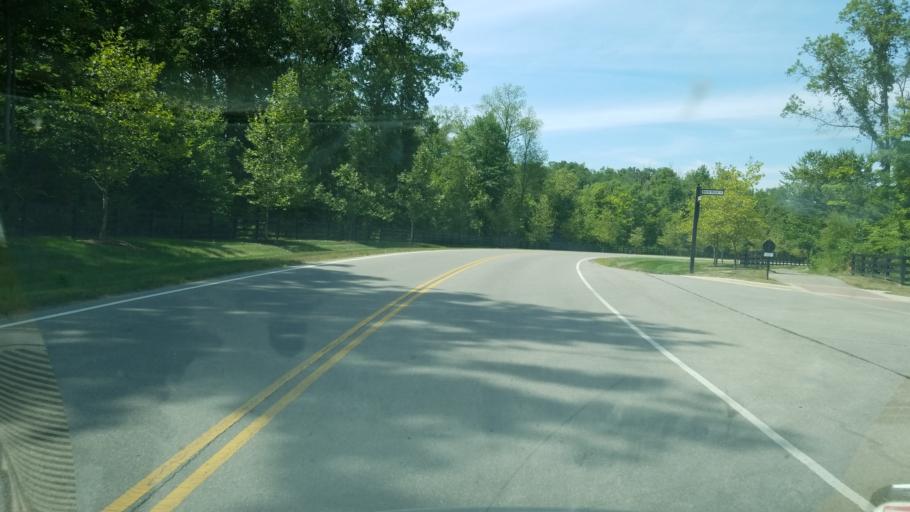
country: US
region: Ohio
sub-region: Union County
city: New California
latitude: 40.1710
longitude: -83.1860
